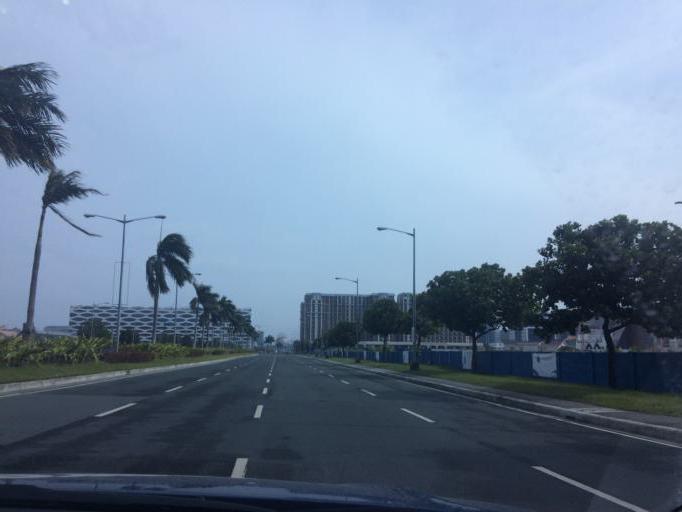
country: PH
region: Metro Manila
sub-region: Makati City
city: Makati City
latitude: 14.5252
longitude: 120.9853
